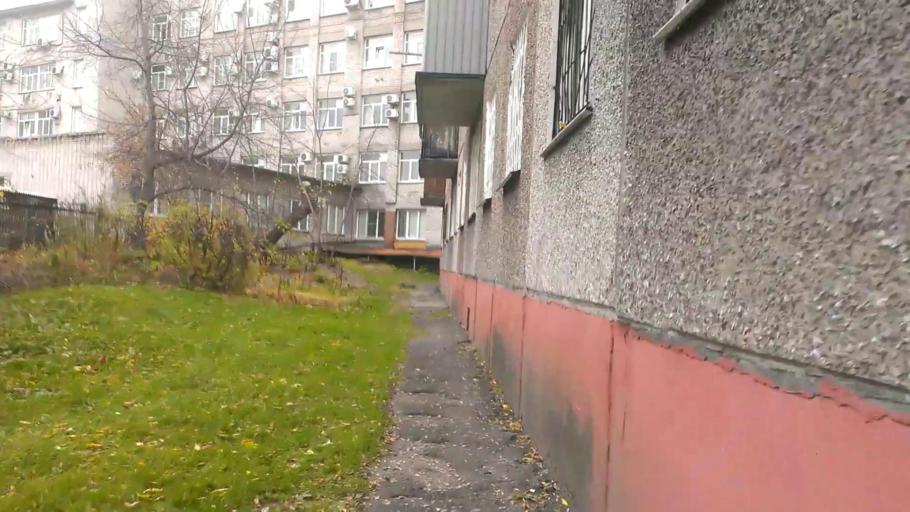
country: RU
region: Altai Krai
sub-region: Gorod Barnaulskiy
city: Barnaul
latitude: 53.3484
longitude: 83.7710
